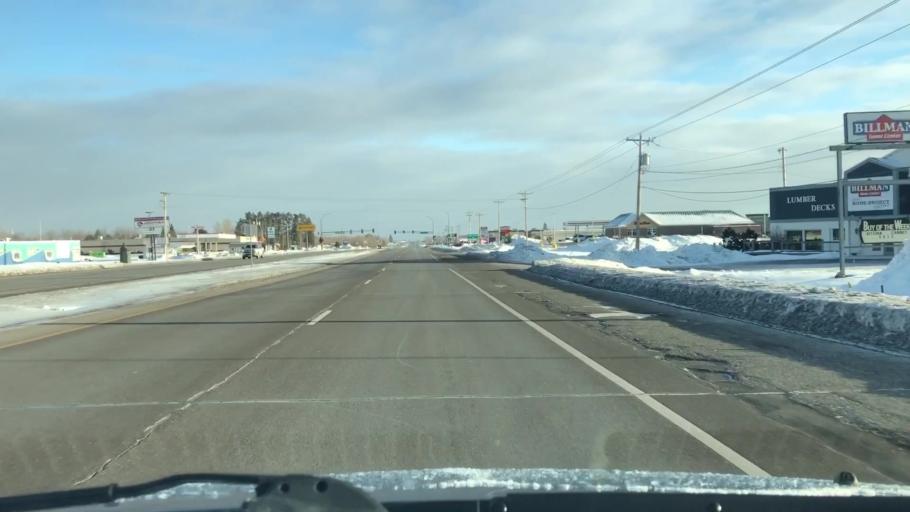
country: US
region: Minnesota
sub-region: Saint Louis County
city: Hermantown
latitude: 46.8354
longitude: -92.2085
